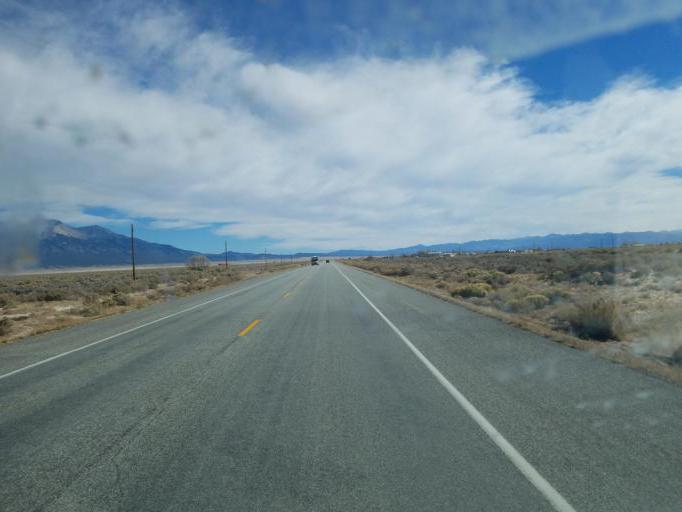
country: US
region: Colorado
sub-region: Alamosa County
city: Alamosa East
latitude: 37.4745
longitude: -105.7162
